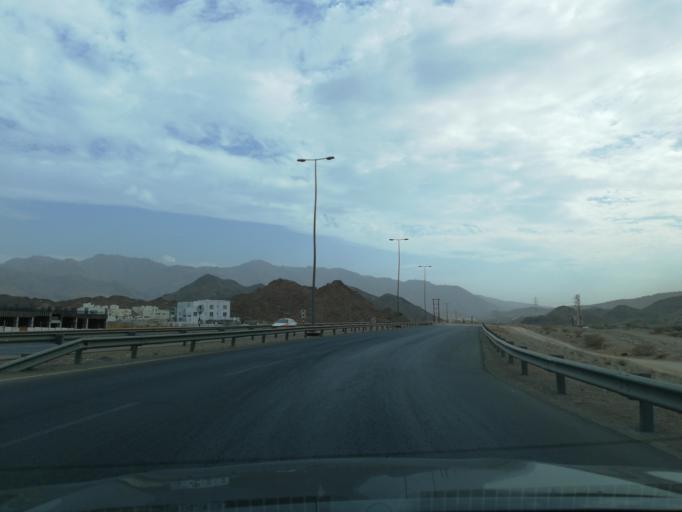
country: OM
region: Muhafazat Masqat
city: Bawshar
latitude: 23.5033
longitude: 58.3327
